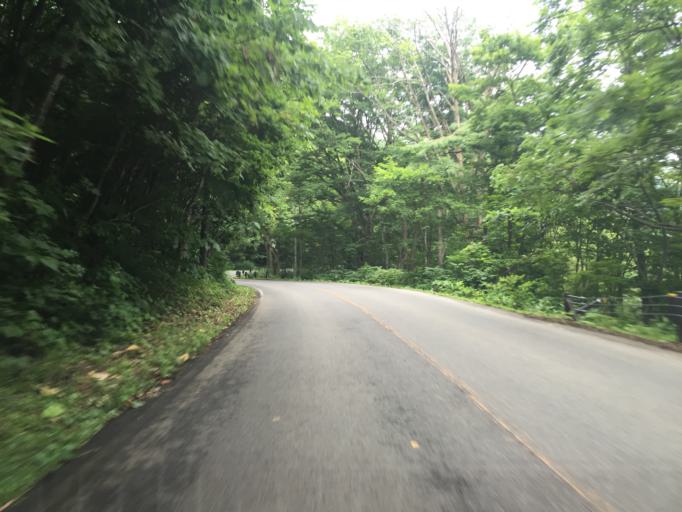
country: JP
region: Fukushima
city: Inawashiro
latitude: 37.7152
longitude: 140.0618
